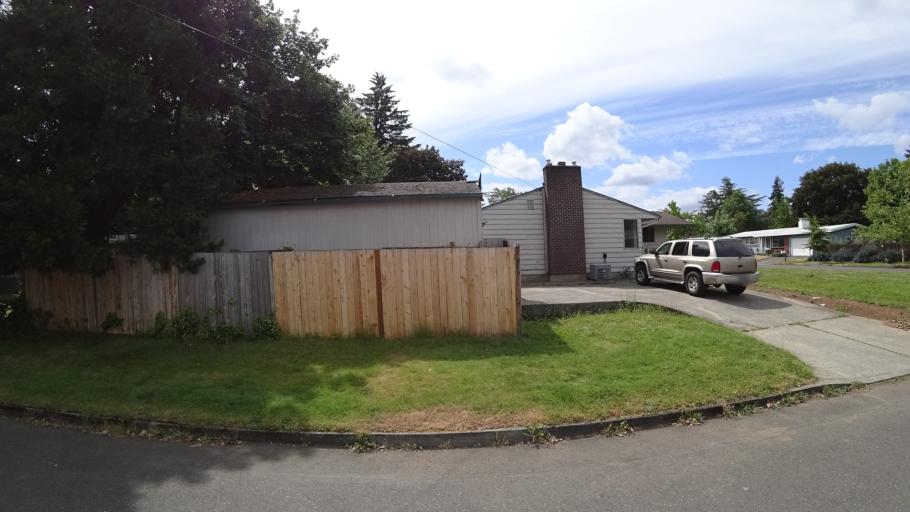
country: US
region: Oregon
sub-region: Multnomah County
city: Lents
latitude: 45.4879
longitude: -122.5514
